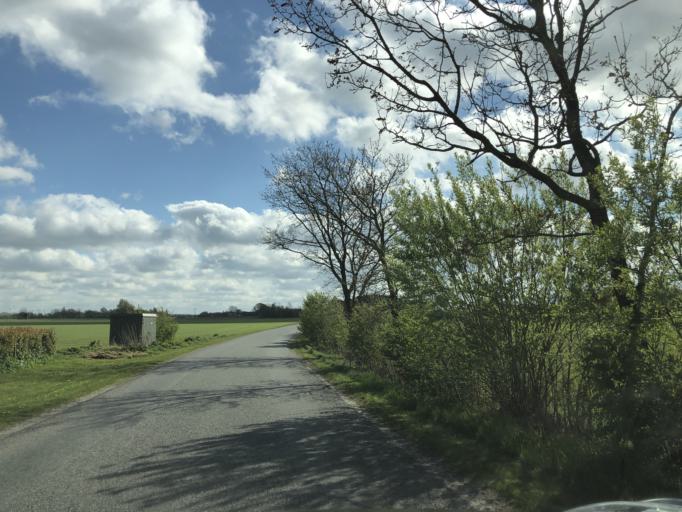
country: DK
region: Central Jutland
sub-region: Herning Kommune
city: Avlum
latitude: 56.2705
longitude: 8.6917
